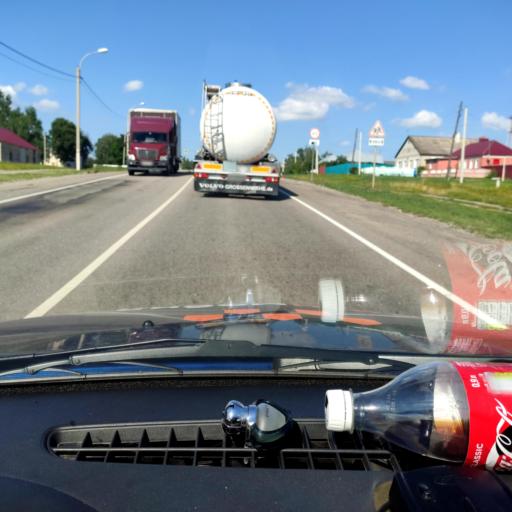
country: RU
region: Lipetsk
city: Kazaki
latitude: 52.6307
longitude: 38.2781
